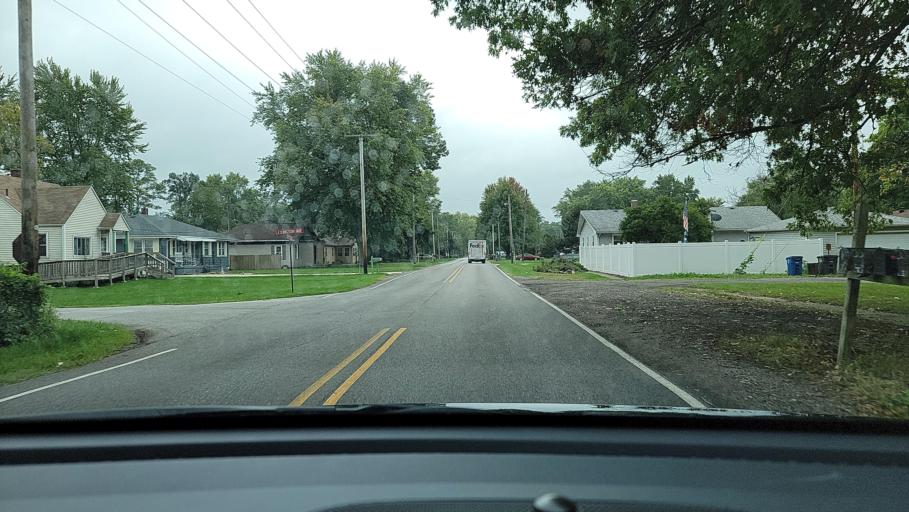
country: US
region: Indiana
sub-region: Lake County
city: Lake Station
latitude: 41.5731
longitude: -87.2220
